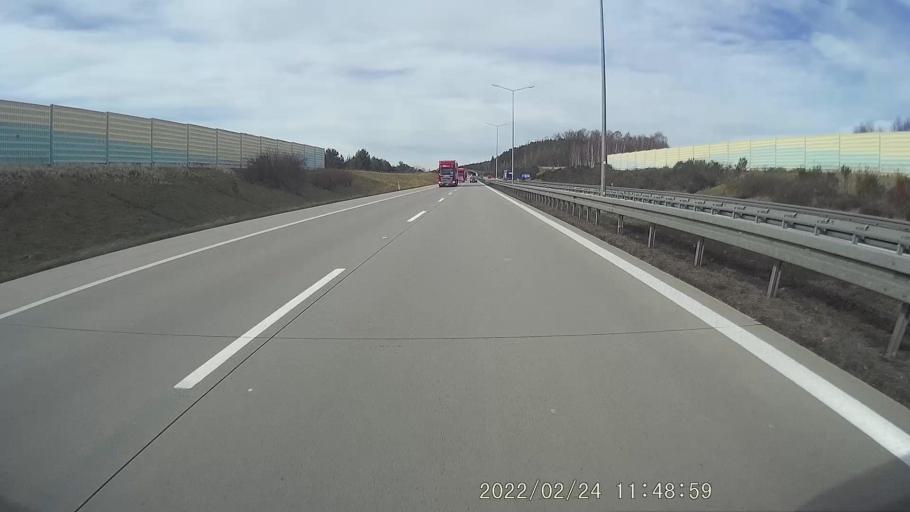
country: PL
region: Lower Silesian Voivodeship
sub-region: Powiat polkowicki
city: Radwanice
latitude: 51.5893
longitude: 15.9585
